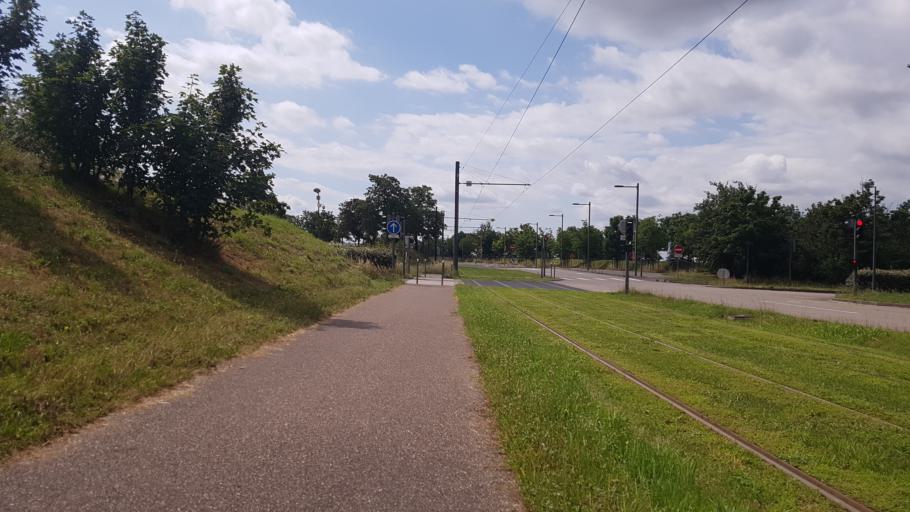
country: FR
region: Rhone-Alpes
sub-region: Departement du Rhone
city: Chassieu
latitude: 45.7347
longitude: 4.9464
